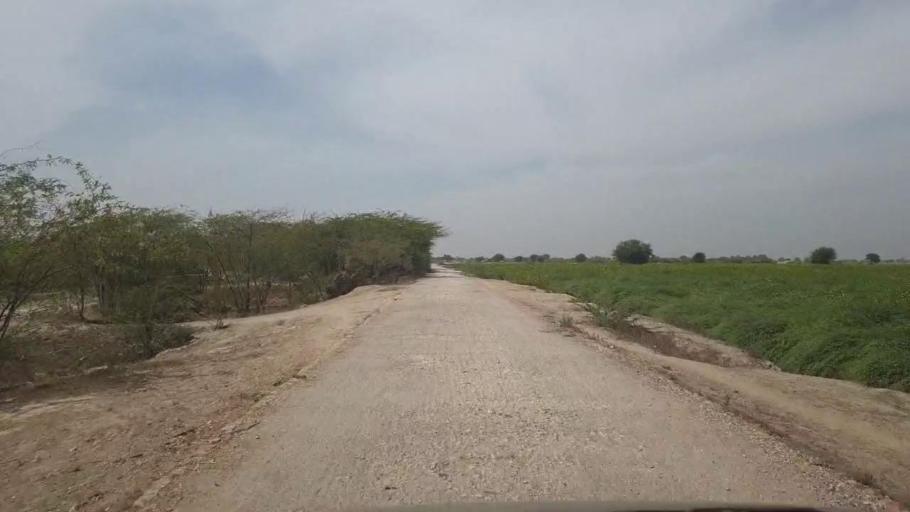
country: PK
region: Sindh
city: Kunri
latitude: 25.2296
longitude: 69.6639
